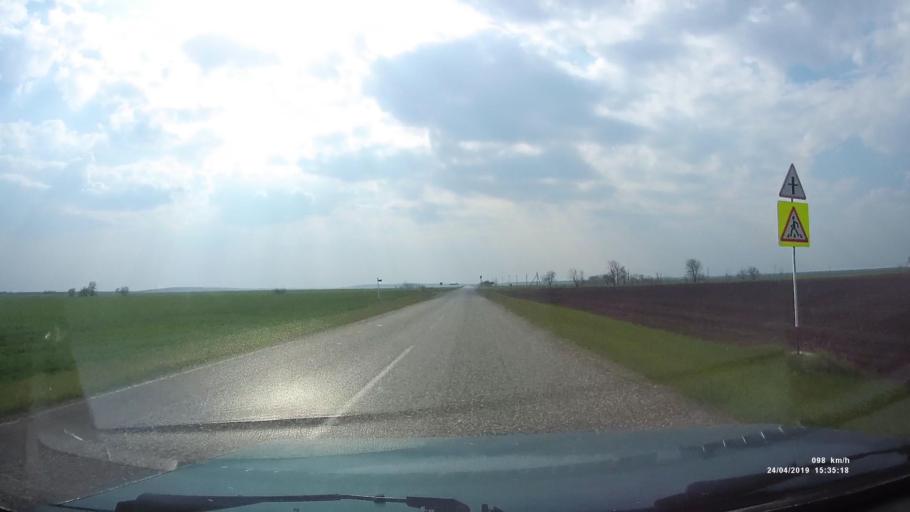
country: RU
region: Kalmykiya
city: Yashalta
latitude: 46.5994
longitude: 42.8971
